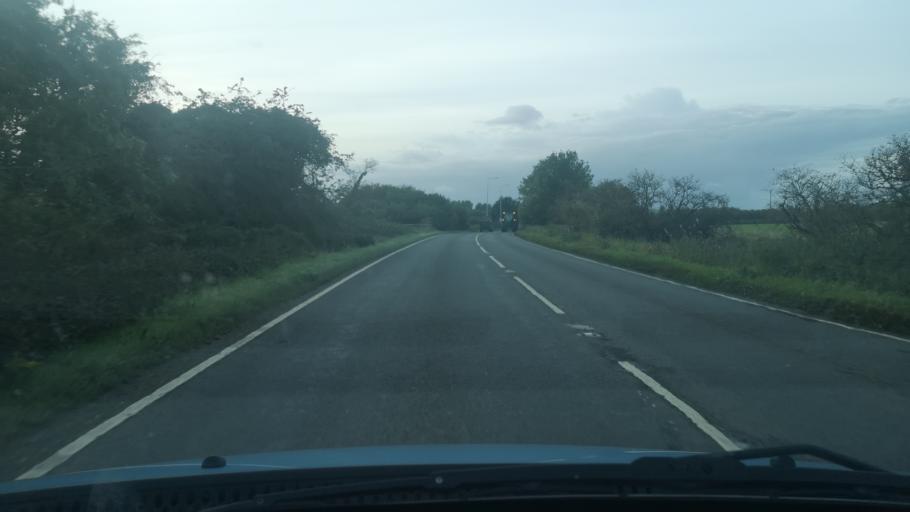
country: GB
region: England
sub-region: North Lincolnshire
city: Crowle
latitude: 53.5831
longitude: -0.8099
